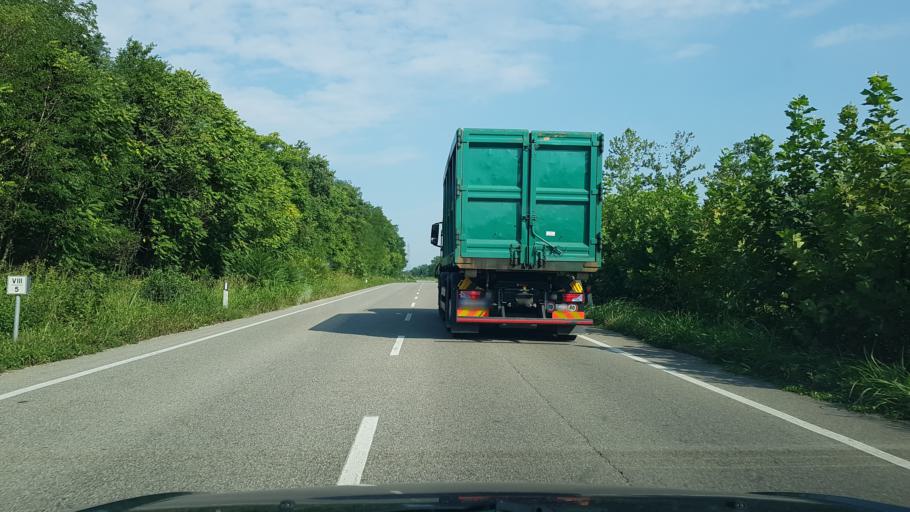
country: IT
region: Friuli Venezia Giulia
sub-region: Provincia di Udine
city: Colloredo di Prato
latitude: 46.0578
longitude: 13.1240
